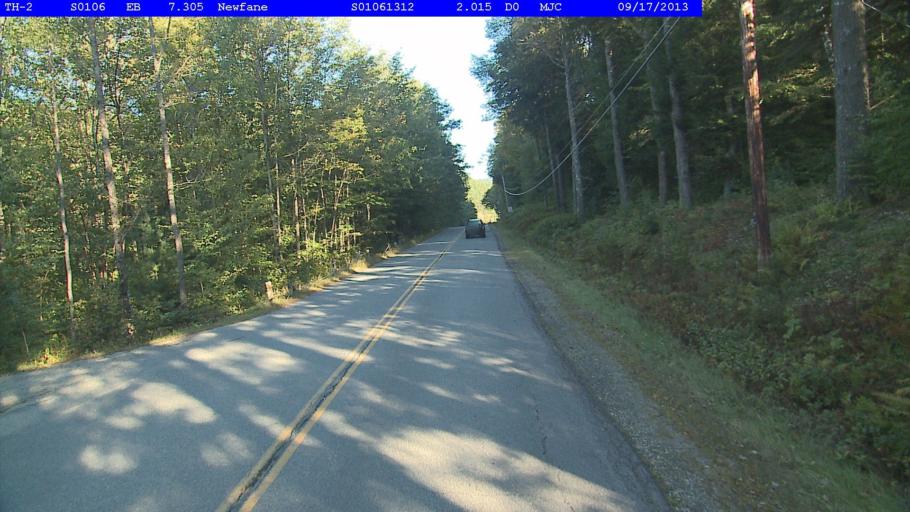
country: US
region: Vermont
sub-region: Windham County
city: Dover
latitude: 42.9458
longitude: -72.7311
